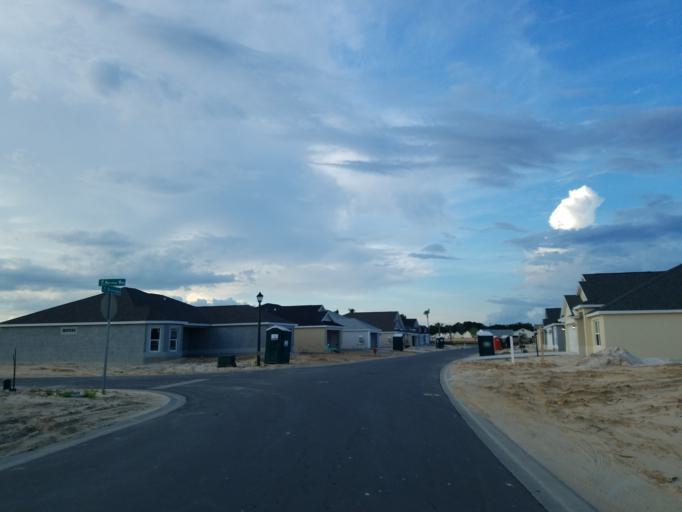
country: US
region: Florida
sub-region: Sumter County
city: Wildwood
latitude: 28.7885
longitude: -82.0146
